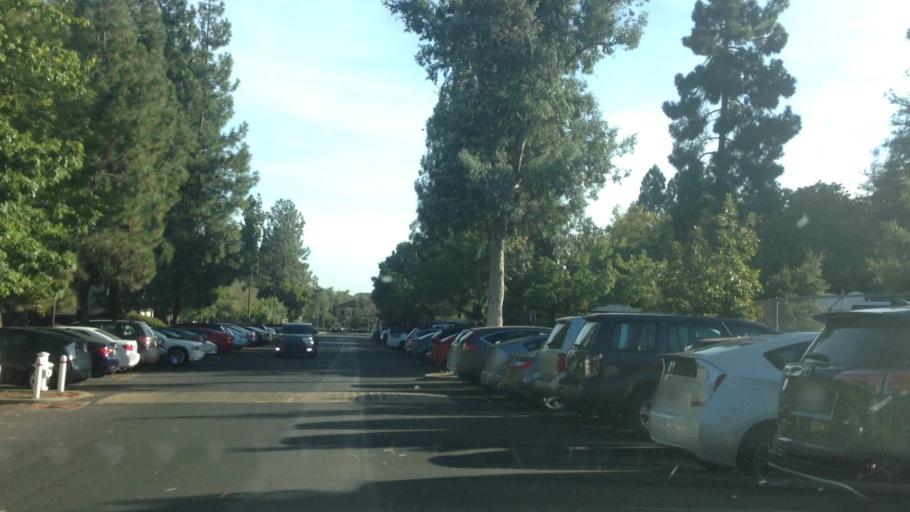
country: US
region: California
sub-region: Santa Clara County
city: Stanford
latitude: 37.4216
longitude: -122.1577
